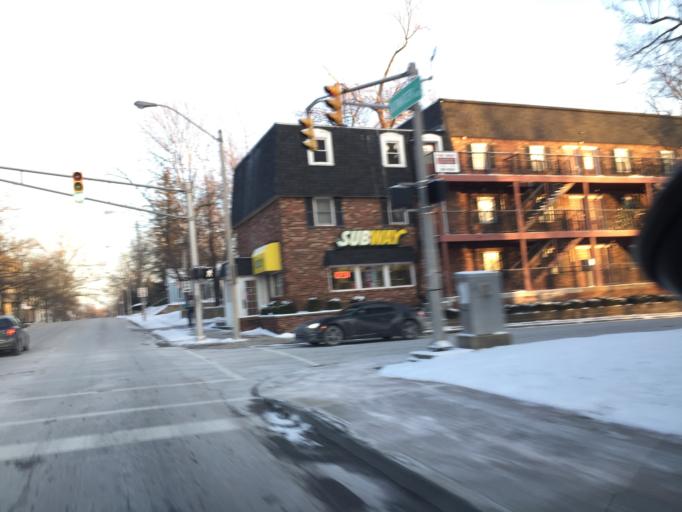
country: US
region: Indiana
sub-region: Monroe County
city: Bloomington
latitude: 39.1631
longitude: -86.5228
